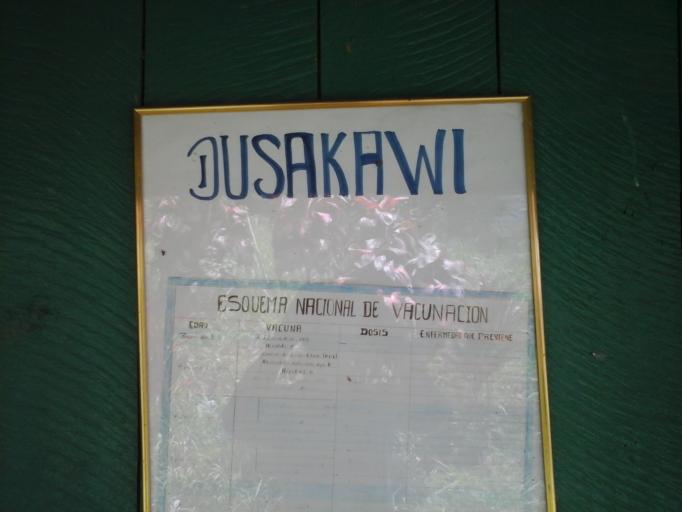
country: CO
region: Cesar
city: Agustin Codazzi
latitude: 9.9627
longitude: -73.0619
